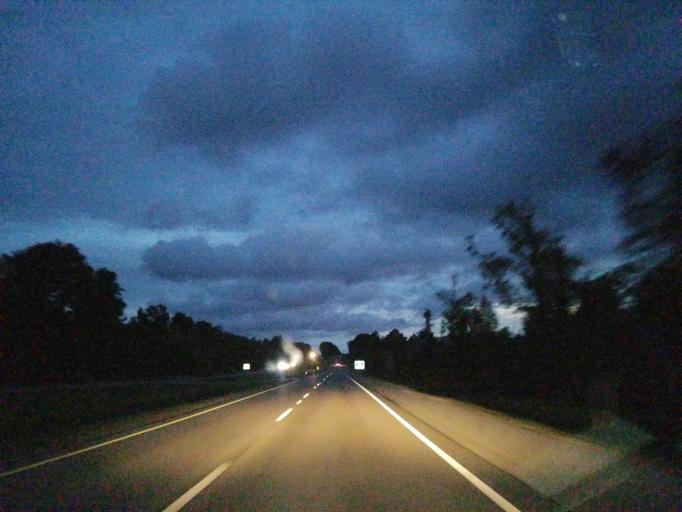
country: US
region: Mississippi
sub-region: Jones County
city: Sharon
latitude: 31.8717
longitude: -89.0459
